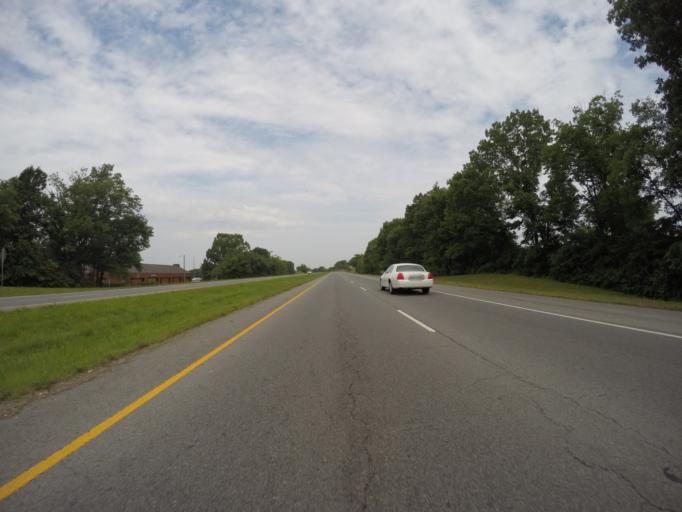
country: US
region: Tennessee
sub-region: Davidson County
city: Lakewood
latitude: 36.2642
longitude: -86.6923
